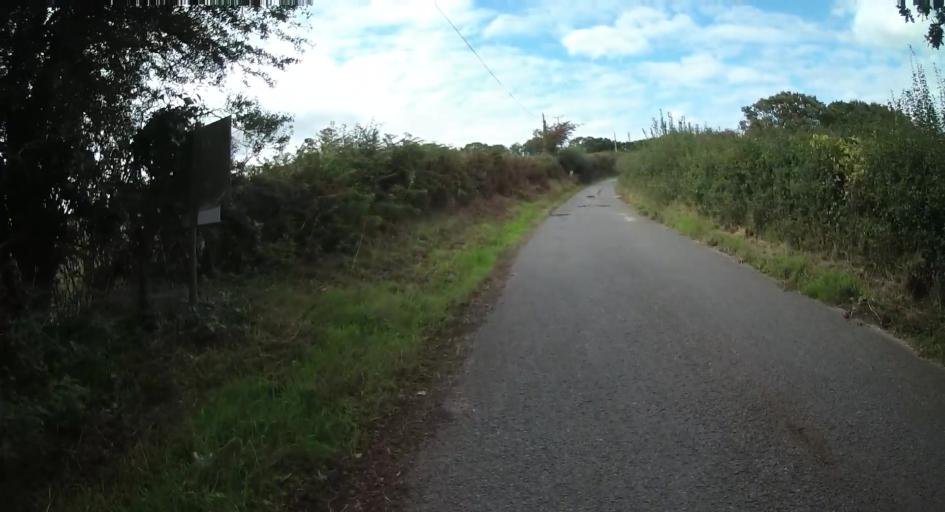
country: GB
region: England
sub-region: Isle of Wight
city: Niton
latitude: 50.6387
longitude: -1.2737
